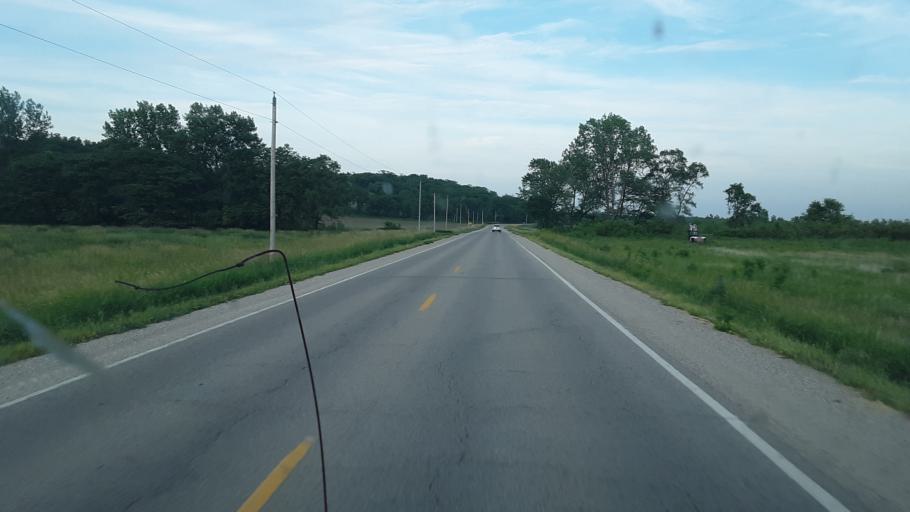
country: US
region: Iowa
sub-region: Benton County
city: Belle Plaine
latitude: 41.9203
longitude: -92.3817
